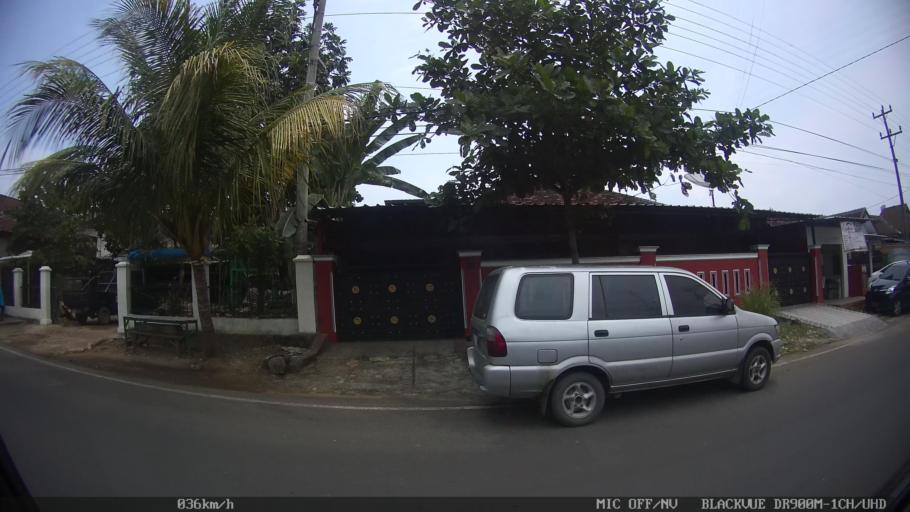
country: ID
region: Lampung
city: Bandarlampung
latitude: -5.4219
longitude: 105.2723
